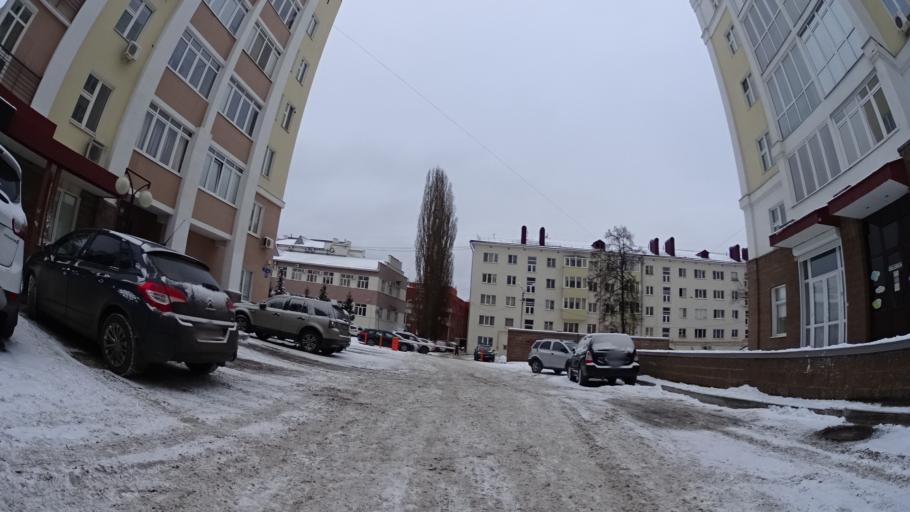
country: RU
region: Bashkortostan
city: Ufa
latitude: 54.7324
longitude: 55.9490
